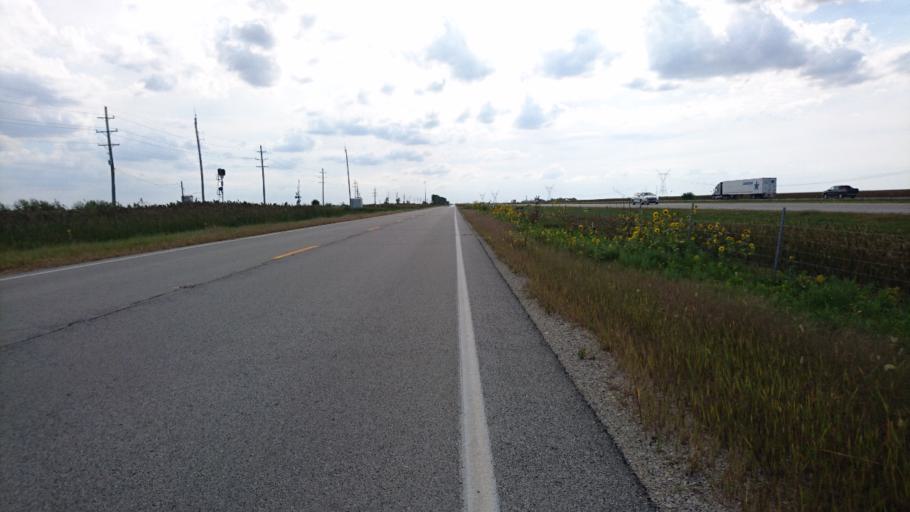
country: US
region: Illinois
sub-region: Grundy County
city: Gardner
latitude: 41.1497
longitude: -88.3566
